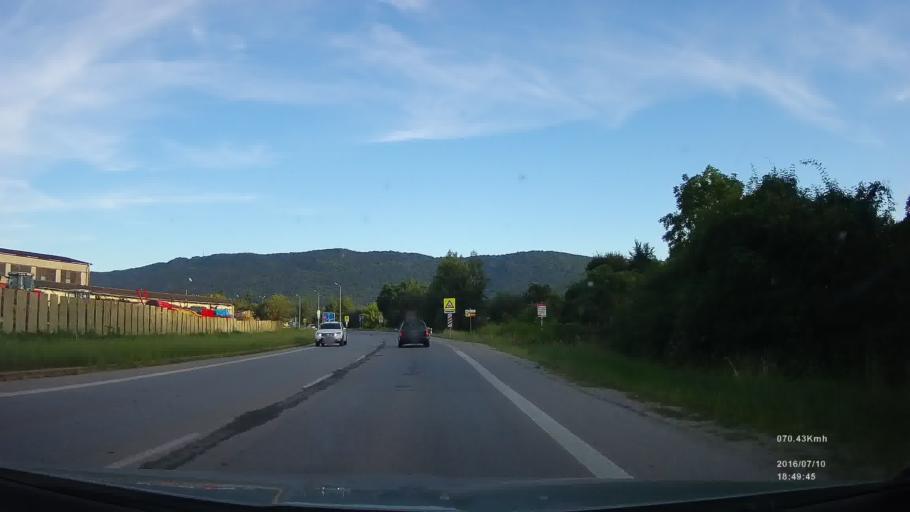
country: SK
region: Kosicky
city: Roznava
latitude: 48.6486
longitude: 20.5225
